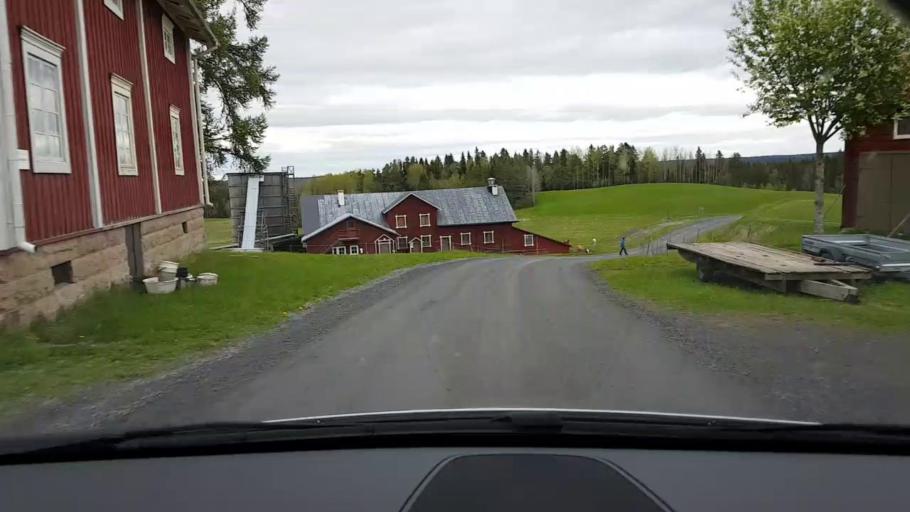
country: SE
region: Jaemtland
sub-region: Krokoms Kommun
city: Krokom
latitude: 63.3224
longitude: 14.4047
